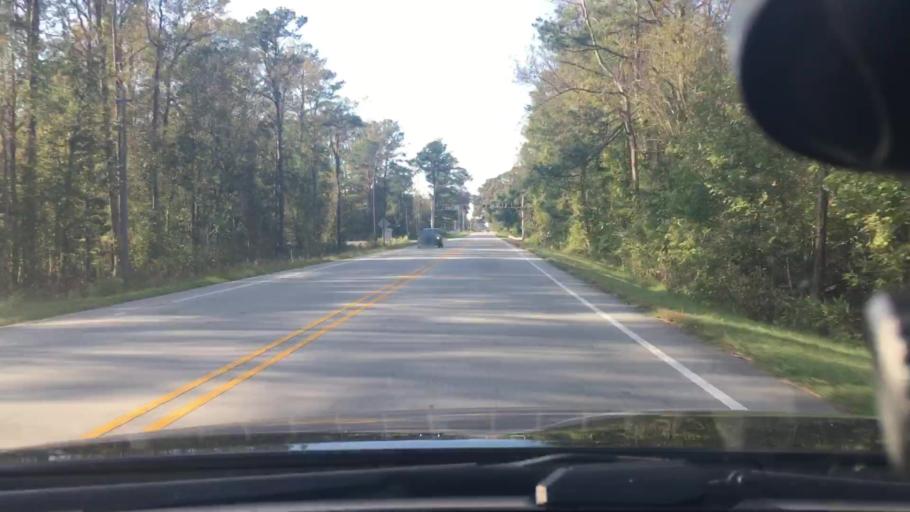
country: US
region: North Carolina
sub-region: Craven County
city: Vanceboro
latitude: 35.2370
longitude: -77.0749
